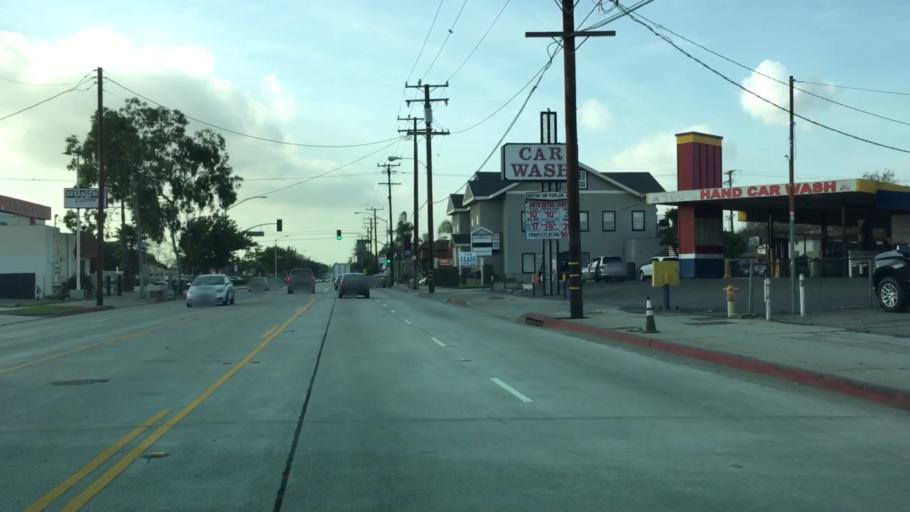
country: US
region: California
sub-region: Los Angeles County
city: Montebello
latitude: 34.0152
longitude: -118.0965
